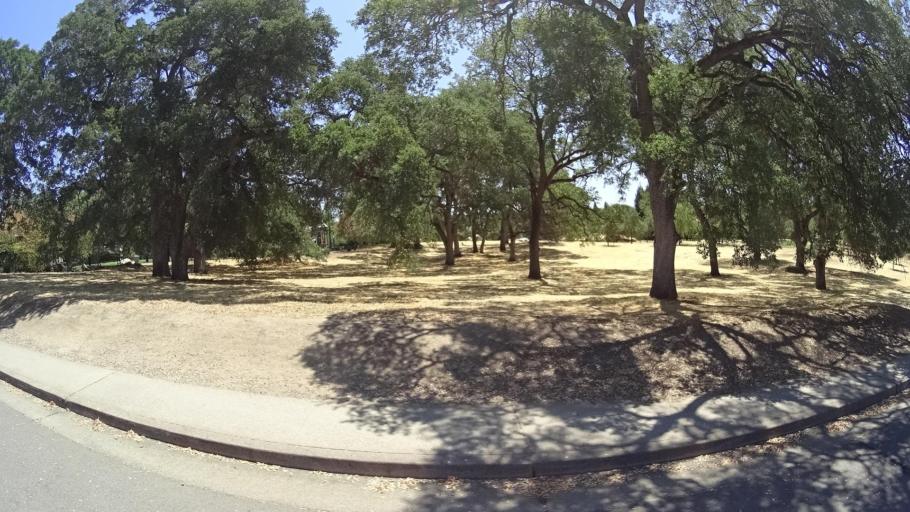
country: US
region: California
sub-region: Placer County
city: Rocklin
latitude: 38.8293
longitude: -121.2550
